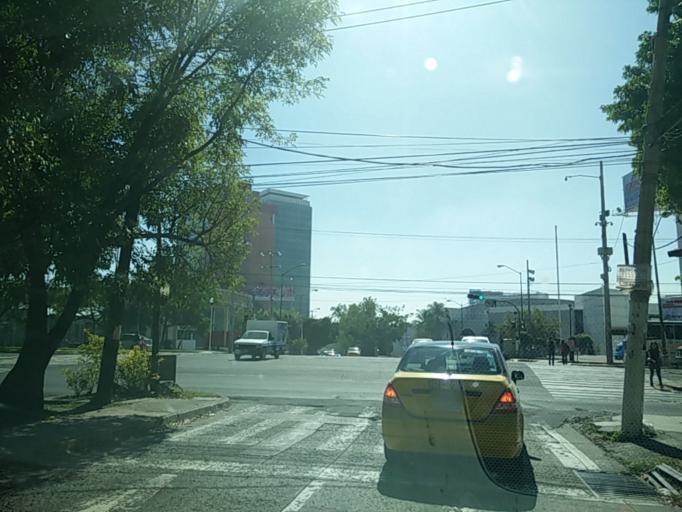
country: MX
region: Jalisco
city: Guadalajara
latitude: 20.6553
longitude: -103.3917
